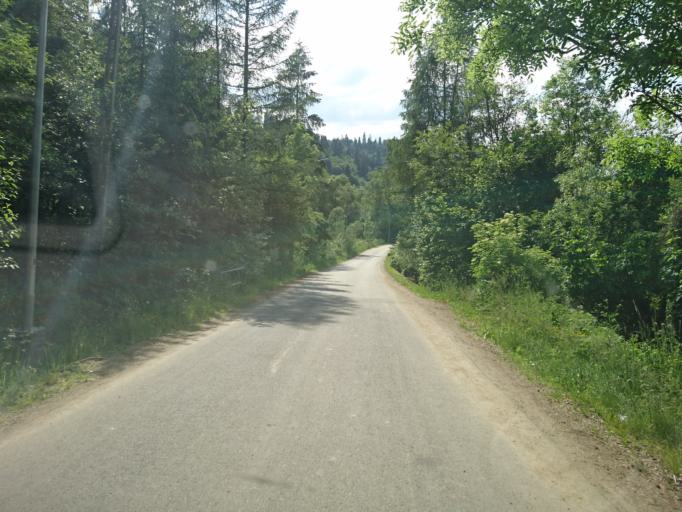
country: PL
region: Lesser Poland Voivodeship
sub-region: Powiat nowotarski
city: Lapsze Nizne
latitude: 49.3961
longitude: 20.2453
